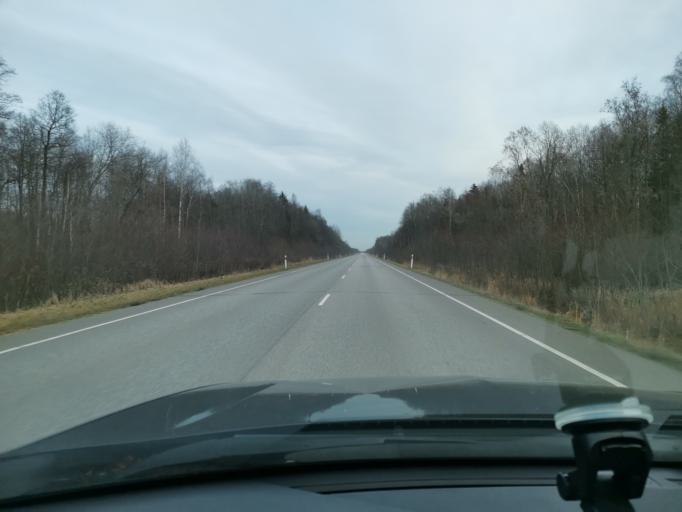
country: EE
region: Ida-Virumaa
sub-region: Narva-Joesuu linn
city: Narva-Joesuu
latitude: 59.3303
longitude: 27.9444
